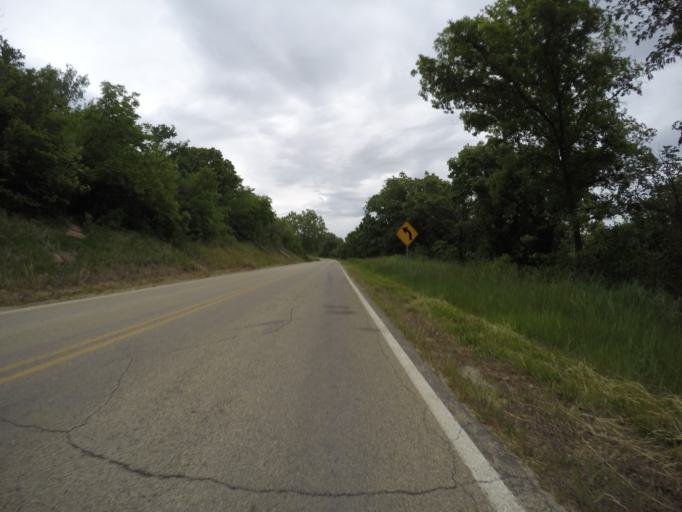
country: US
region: Kansas
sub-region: Pottawatomie County
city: Wamego
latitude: 39.1831
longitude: -96.4033
